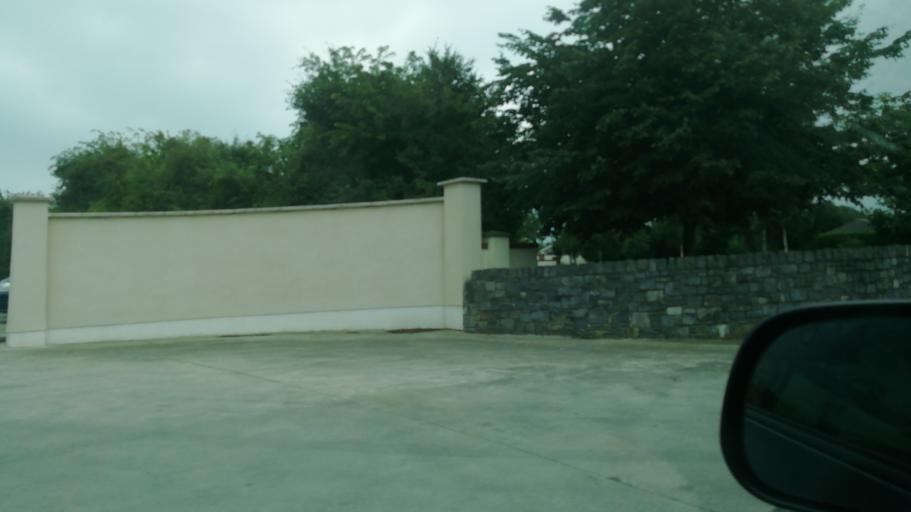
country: IE
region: Munster
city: Fethard
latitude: 52.4727
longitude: -7.6918
